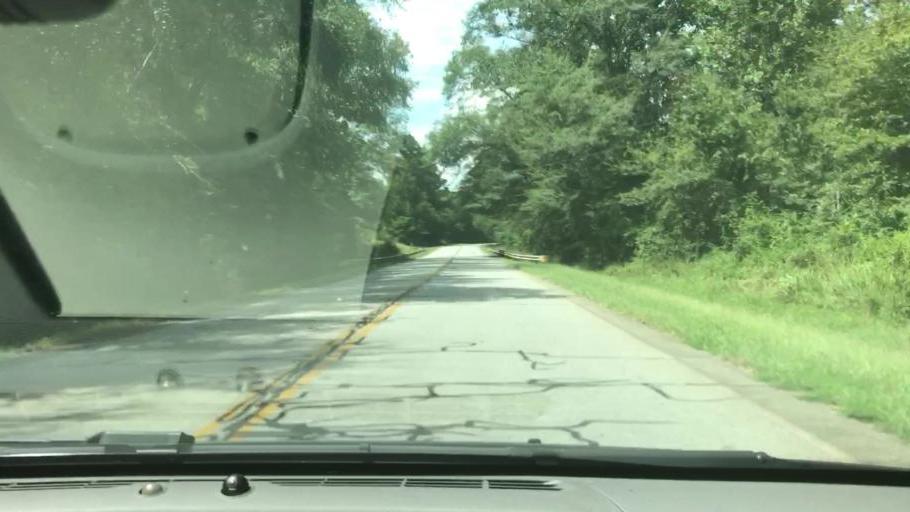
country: US
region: Georgia
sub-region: Stewart County
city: Lumpkin
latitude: 32.1458
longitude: -84.8904
